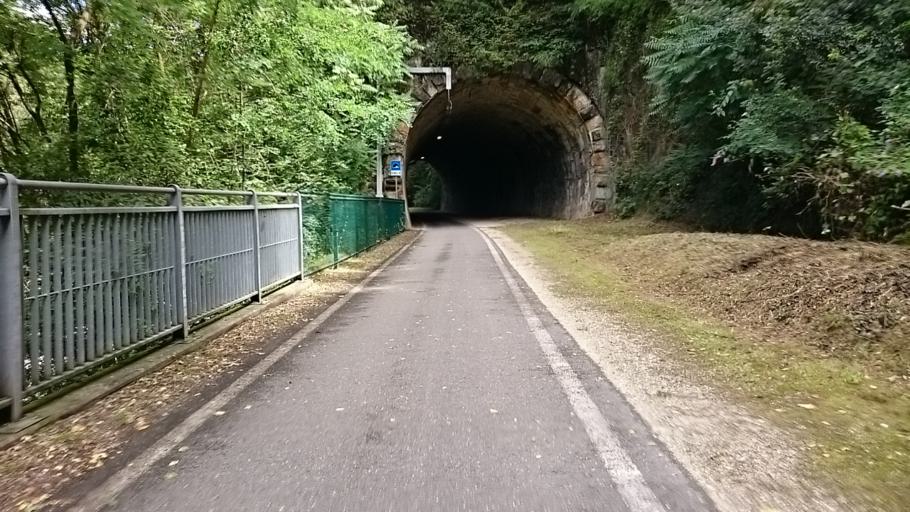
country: IT
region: Trentino-Alto Adige
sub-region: Bolzano
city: Fie Allo Sciliar
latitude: 46.5187
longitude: 11.4820
